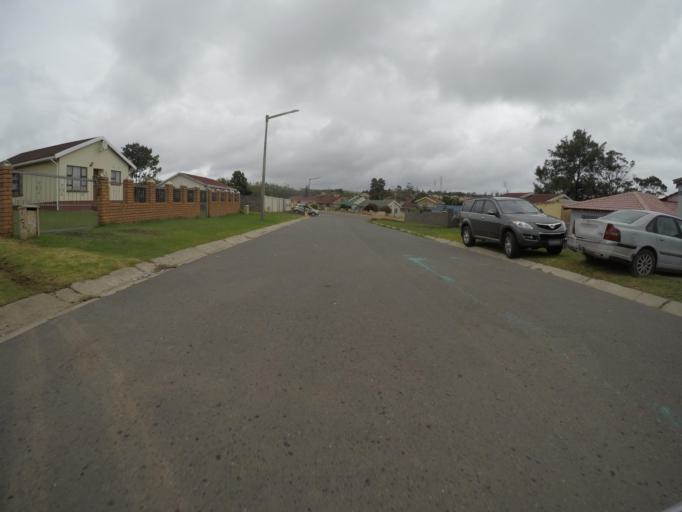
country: ZA
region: Eastern Cape
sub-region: Buffalo City Metropolitan Municipality
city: East London
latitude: -32.9943
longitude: 27.8390
